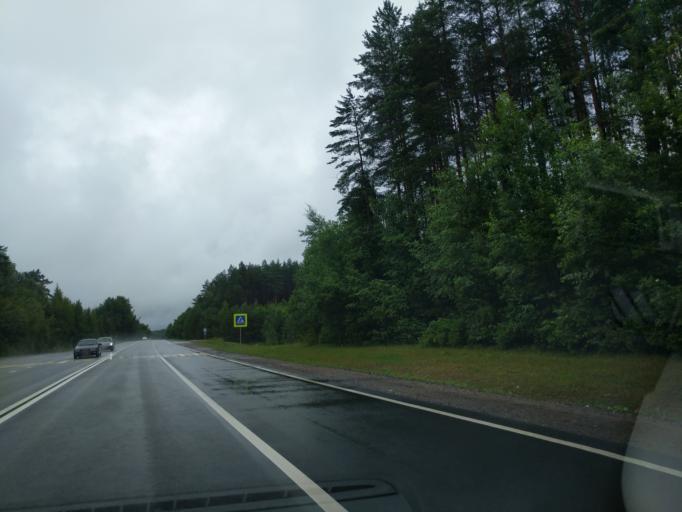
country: BY
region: Minsk
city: Syomkava
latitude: 54.1750
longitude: 27.4996
